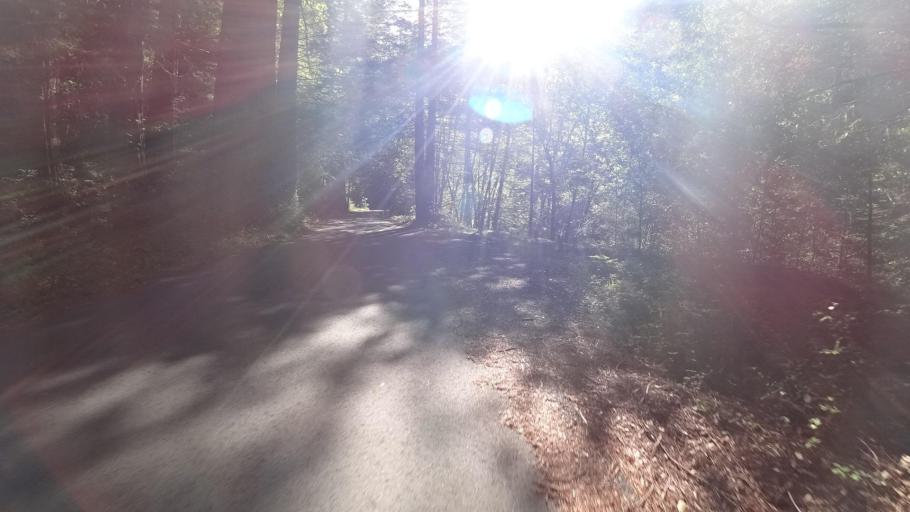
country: US
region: California
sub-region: Humboldt County
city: Rio Dell
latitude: 40.3524
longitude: -123.9811
